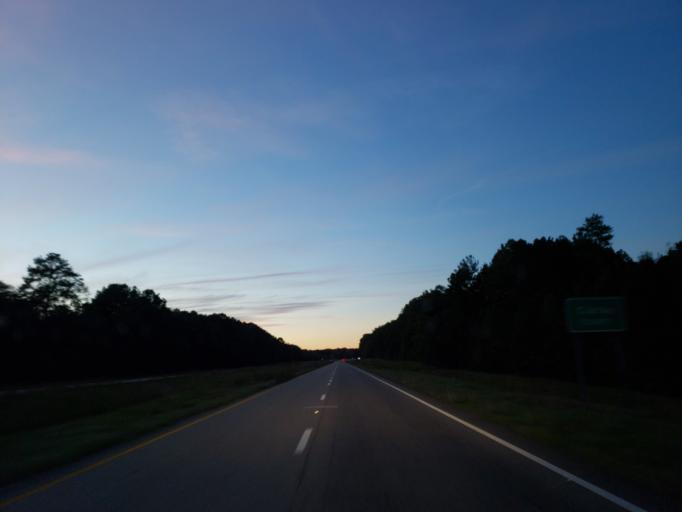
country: US
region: Mississippi
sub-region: Wayne County
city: Waynesboro
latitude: 31.8436
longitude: -88.7100
